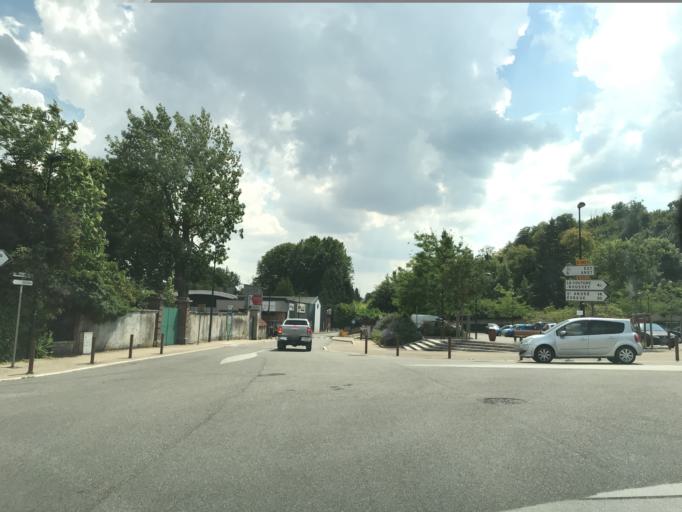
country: FR
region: Haute-Normandie
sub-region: Departement de l'Eure
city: Ivry-la-Bataille
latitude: 48.8826
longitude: 1.4586
